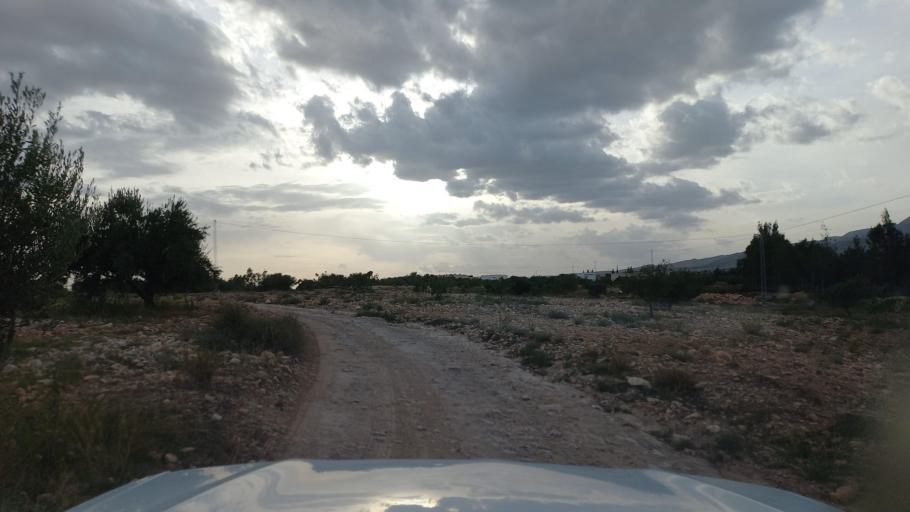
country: TN
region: Al Qasrayn
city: Sbiba
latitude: 35.4399
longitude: 9.0991
